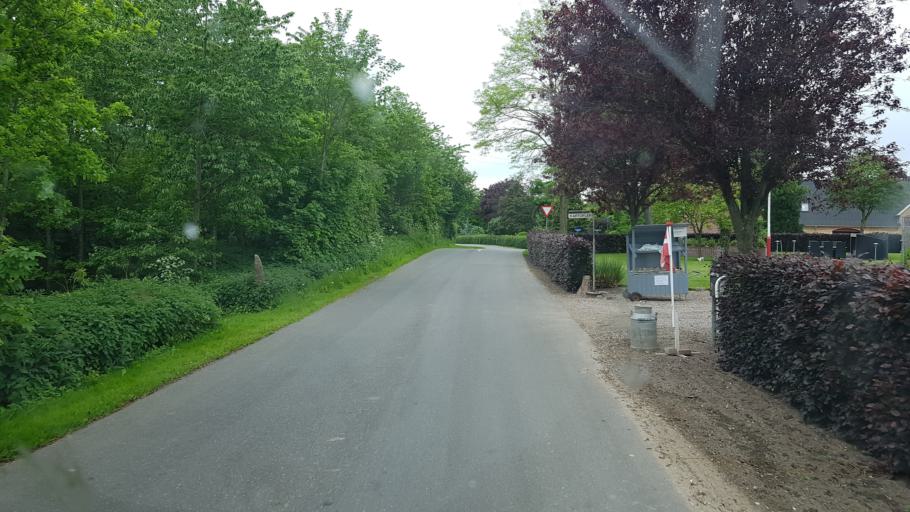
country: DK
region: South Denmark
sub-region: Middelfart Kommune
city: Brenderup
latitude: 55.4736
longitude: 10.0670
